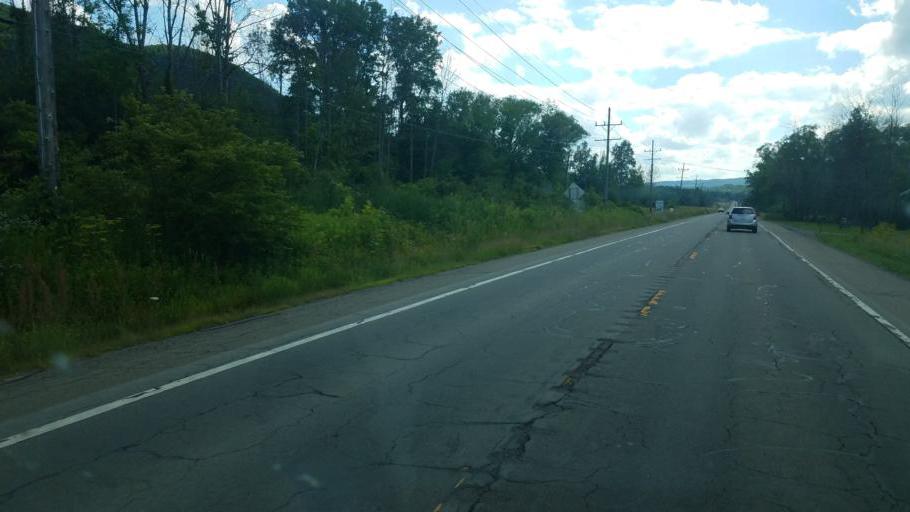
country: US
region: New York
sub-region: Steuben County
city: Bath
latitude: 42.3960
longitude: -77.2365
